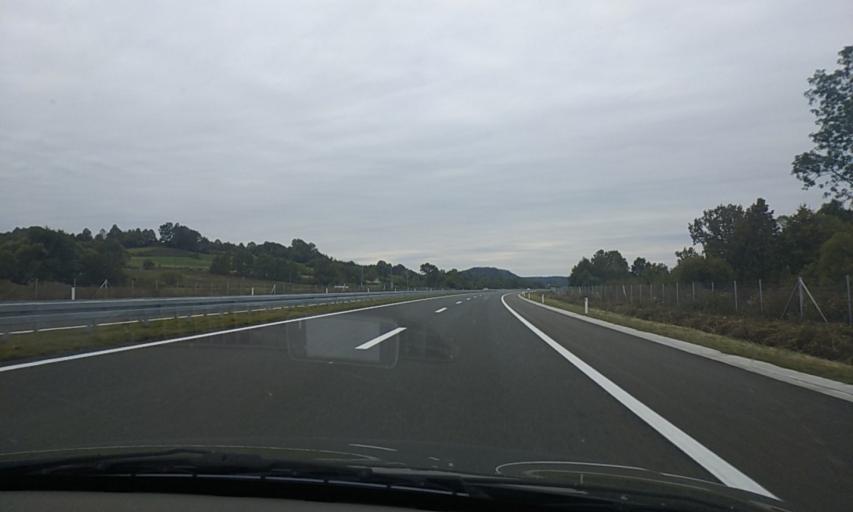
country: BA
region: Republika Srpska
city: Prnjavor
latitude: 44.8762
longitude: 17.6266
